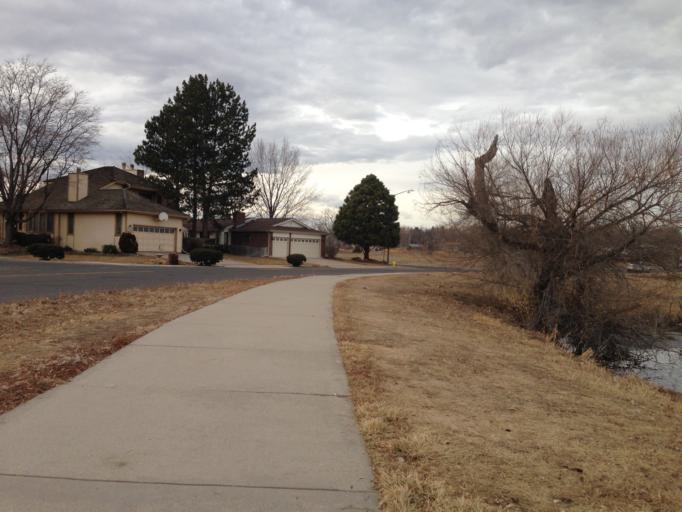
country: US
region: Colorado
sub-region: Adams County
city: Westminster
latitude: 39.8430
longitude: -105.0705
